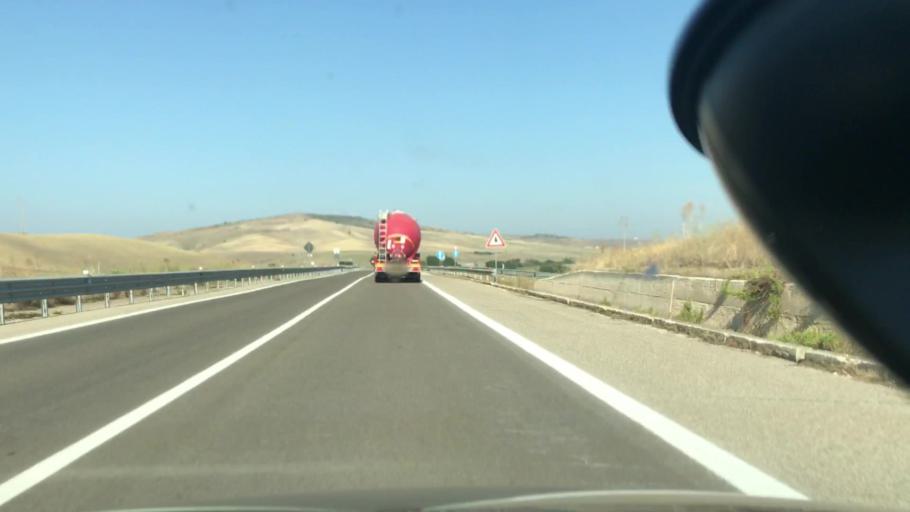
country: IT
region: Basilicate
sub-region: Provincia di Matera
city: Irsina
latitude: 40.7875
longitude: 16.2914
